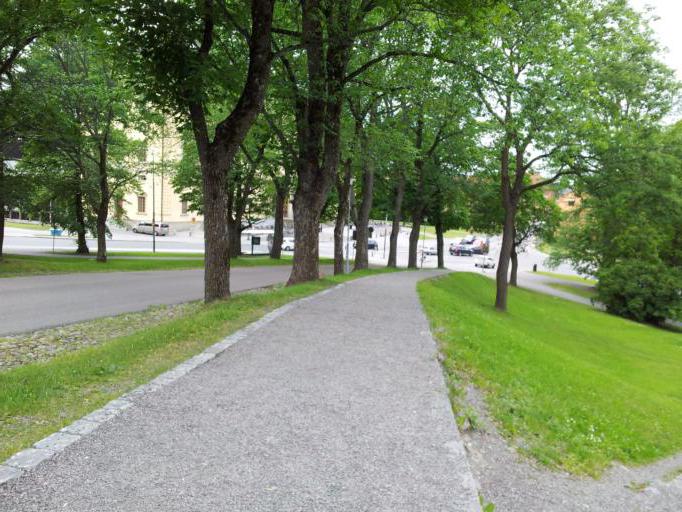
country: SE
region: Uppsala
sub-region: Uppsala Kommun
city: Uppsala
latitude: 59.8548
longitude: 17.6336
